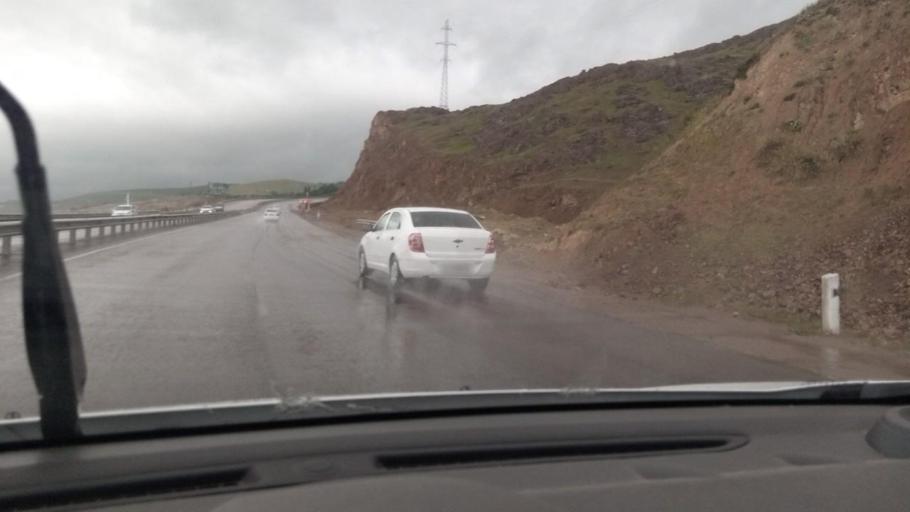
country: UZ
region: Toshkent
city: Angren
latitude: 41.0720
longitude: 70.2744
